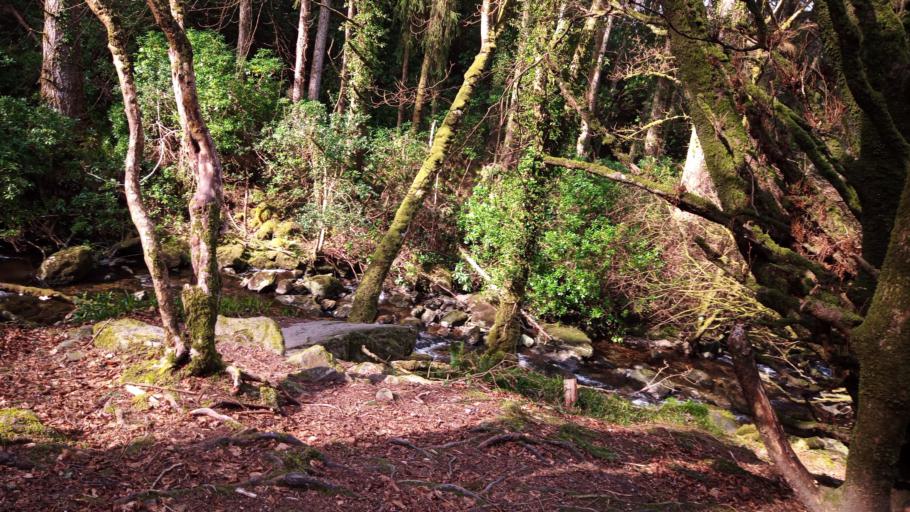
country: IE
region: Munster
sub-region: Ciarrai
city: Cill Airne
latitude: 52.0047
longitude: -9.5062
